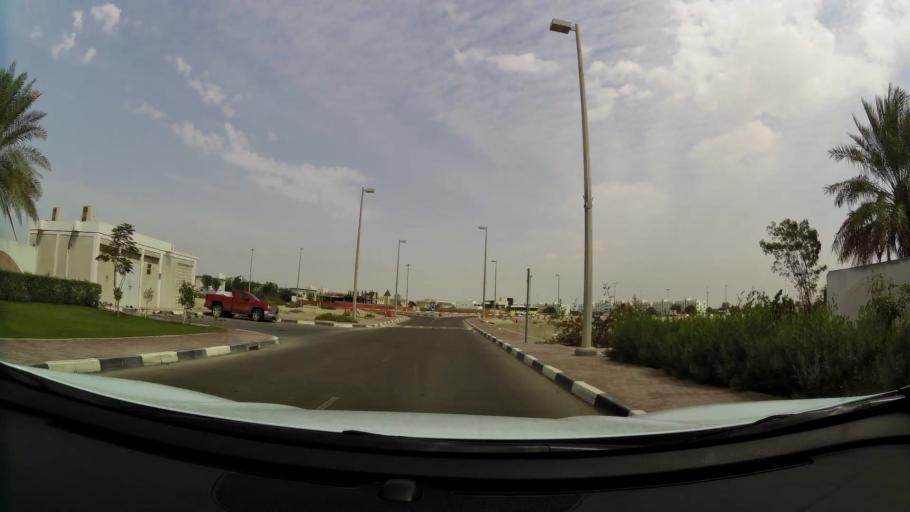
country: AE
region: Abu Dhabi
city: Abu Dhabi
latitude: 24.5221
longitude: 54.6868
